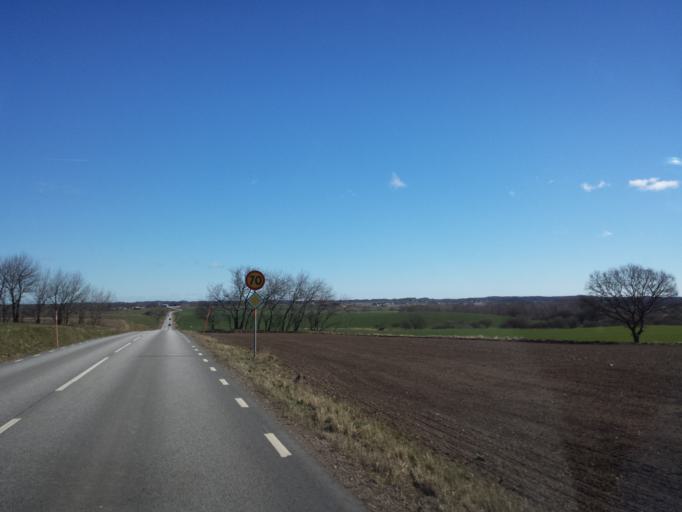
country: SE
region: Skane
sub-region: Tomelilla Kommun
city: Tomelilla
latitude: 55.6257
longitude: 13.8568
